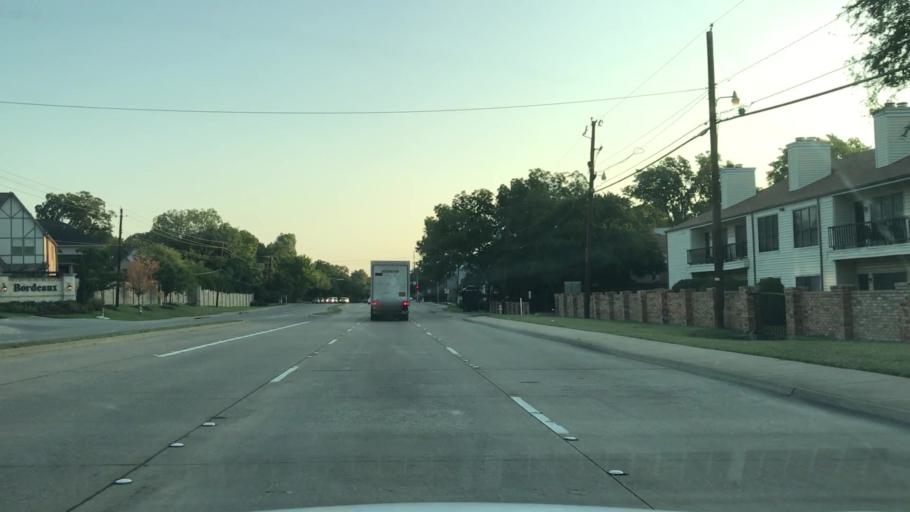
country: US
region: Texas
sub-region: Dallas County
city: Richardson
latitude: 32.8840
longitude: -96.7340
